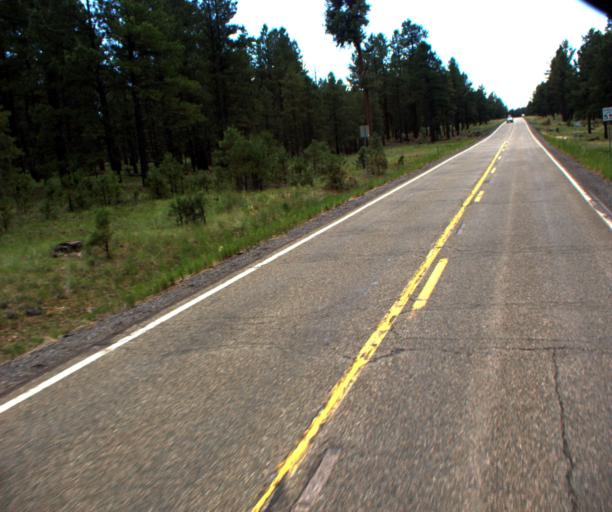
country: US
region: Arizona
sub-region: Coconino County
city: Parks
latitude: 35.3727
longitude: -111.7902
